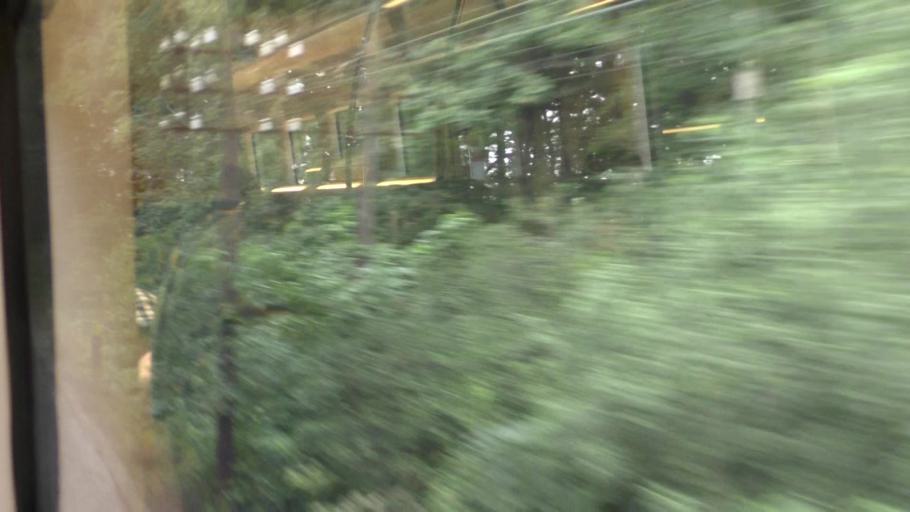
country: DE
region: Saxony
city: Horka
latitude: 51.2701
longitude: 14.9084
